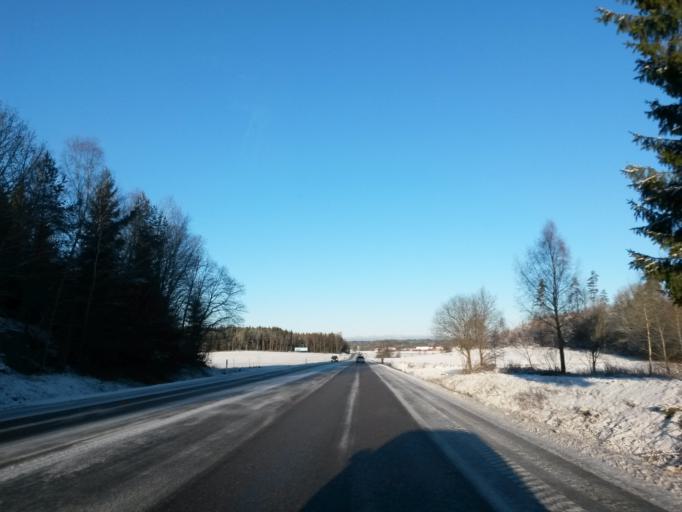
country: SE
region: Vaestra Goetaland
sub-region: Vargarda Kommun
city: Vargarda
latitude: 58.0639
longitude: 12.8178
